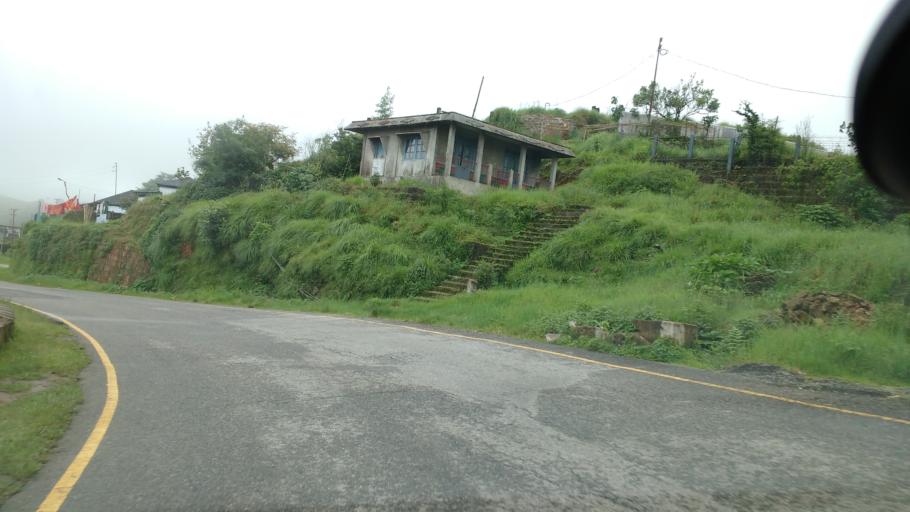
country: IN
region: Meghalaya
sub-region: East Khasi Hills
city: Cherrapunji
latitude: 25.2804
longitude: 91.7292
